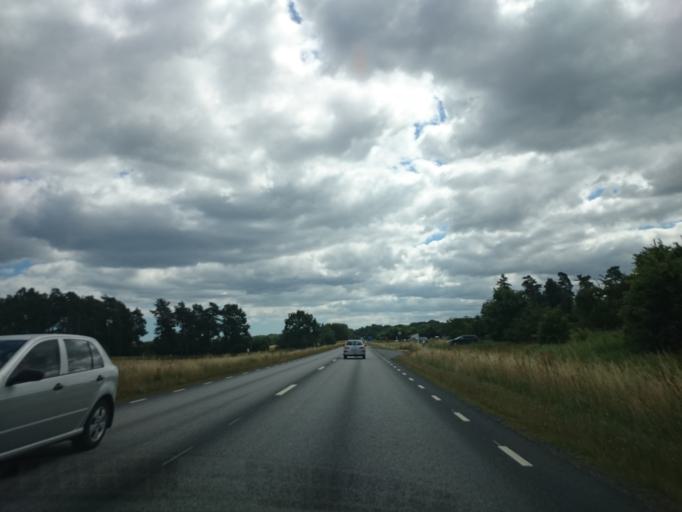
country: SE
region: Skane
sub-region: Kristianstads Kommun
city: Degeberga
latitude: 55.8109
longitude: 14.1388
